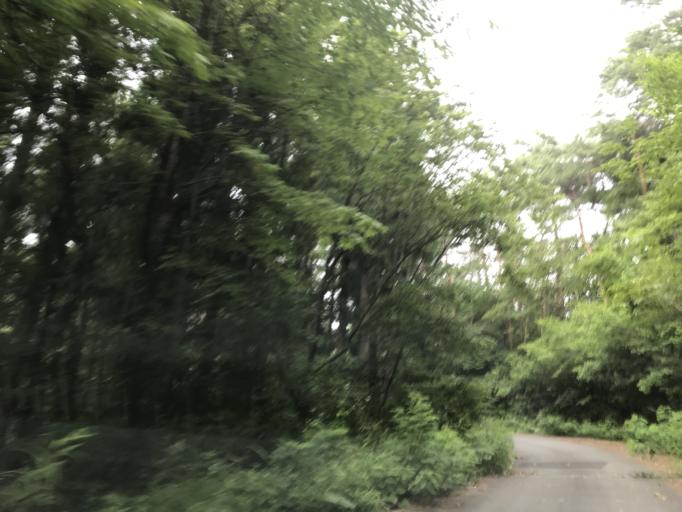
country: JP
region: Iwate
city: Ichinoseki
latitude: 38.8282
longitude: 141.2181
